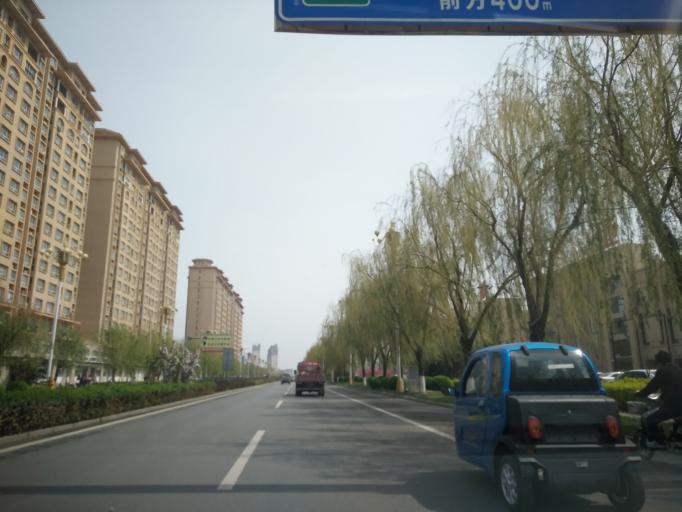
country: CN
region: Beijing
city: Xiji
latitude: 39.7457
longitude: 116.9818
